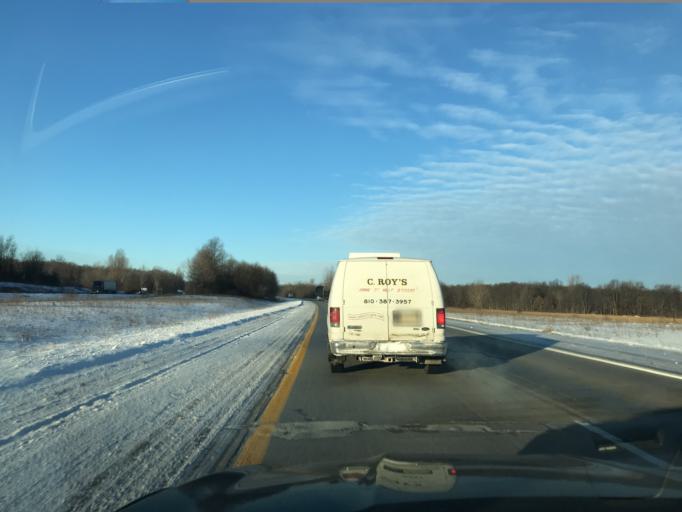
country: US
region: Michigan
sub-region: Lapeer County
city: Imlay City
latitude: 43.0104
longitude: -83.1852
